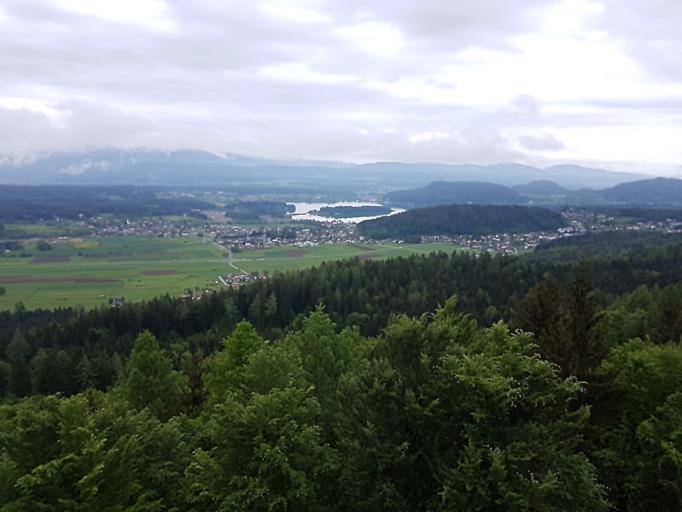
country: AT
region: Carinthia
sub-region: Politischer Bezirk Villach Land
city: Finkenstein am Faaker See
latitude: 46.5466
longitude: 13.9032
